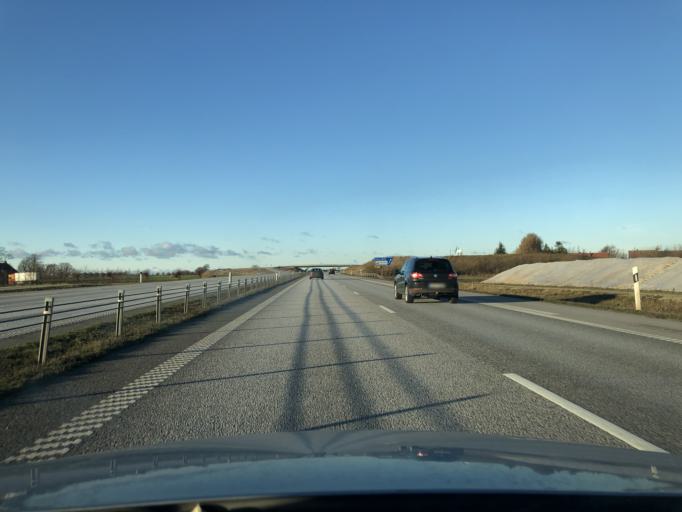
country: SE
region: Skane
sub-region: Vellinge Kommun
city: Vellinge
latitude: 55.4499
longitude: 13.0247
